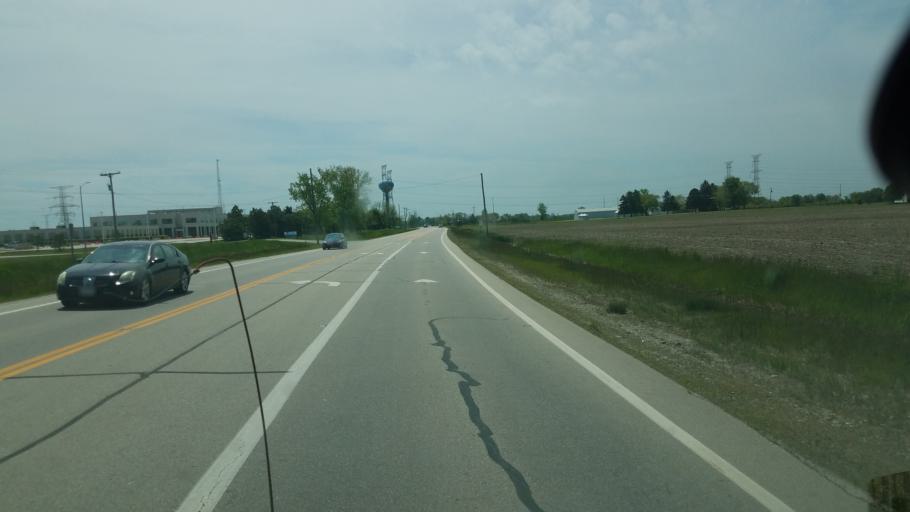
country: US
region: Ohio
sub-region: Ottawa County
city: Oak Harbor
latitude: 41.5994
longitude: -83.0968
